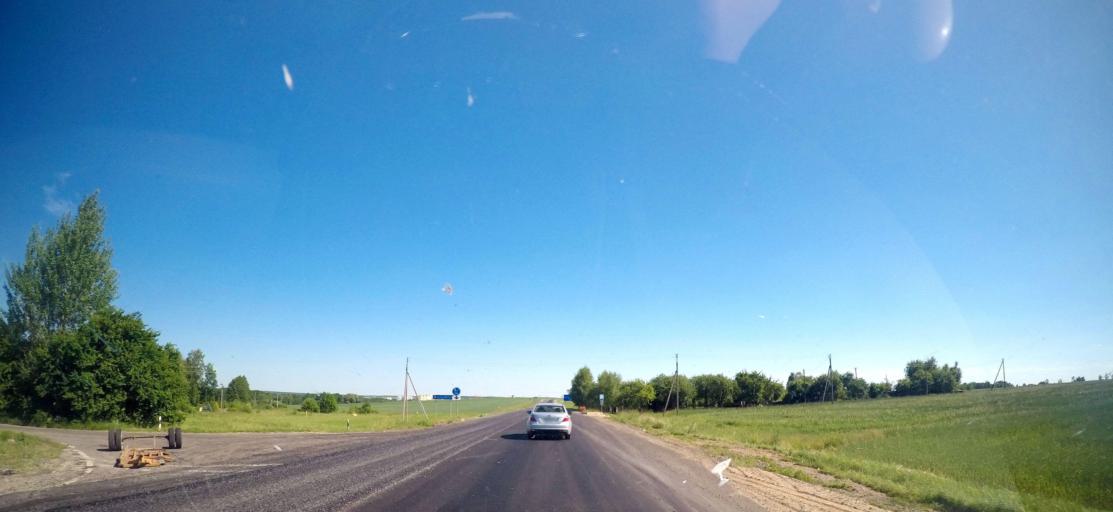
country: BY
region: Grodnenskaya
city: Vyalikaya Byerastavitsa
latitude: 53.2122
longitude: 24.0031
